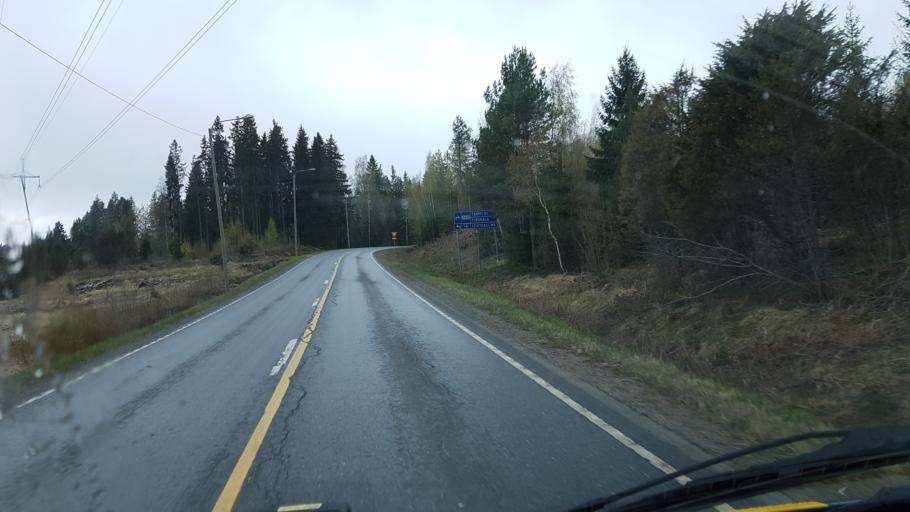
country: FI
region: Pirkanmaa
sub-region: Tampere
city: Pirkkala
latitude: 61.4290
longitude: 23.6257
